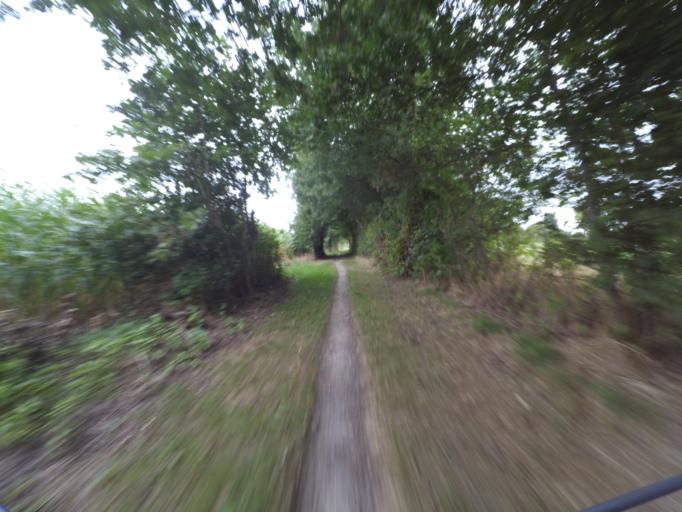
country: DE
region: Lower Saxony
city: Isterberg
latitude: 52.3264
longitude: 7.0817
